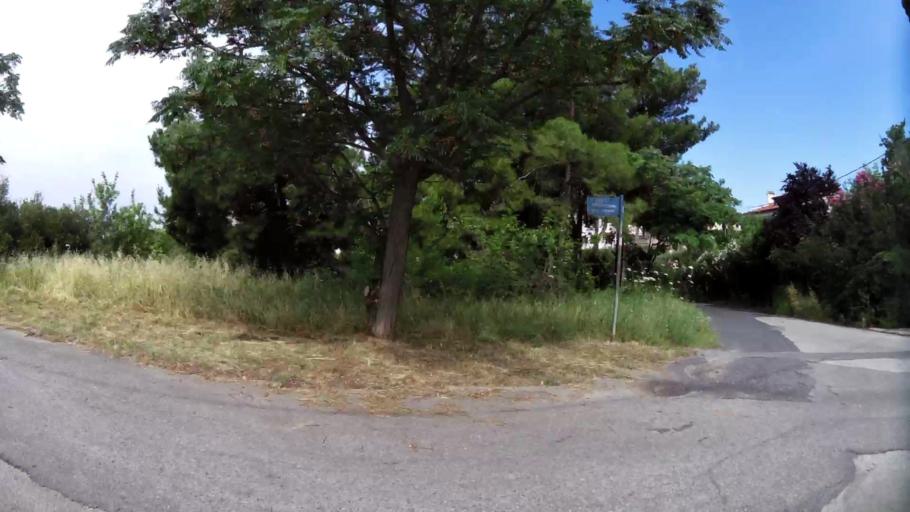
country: GR
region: Central Macedonia
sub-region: Nomos Thessalonikis
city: Panorama
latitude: 40.5795
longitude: 23.0093
